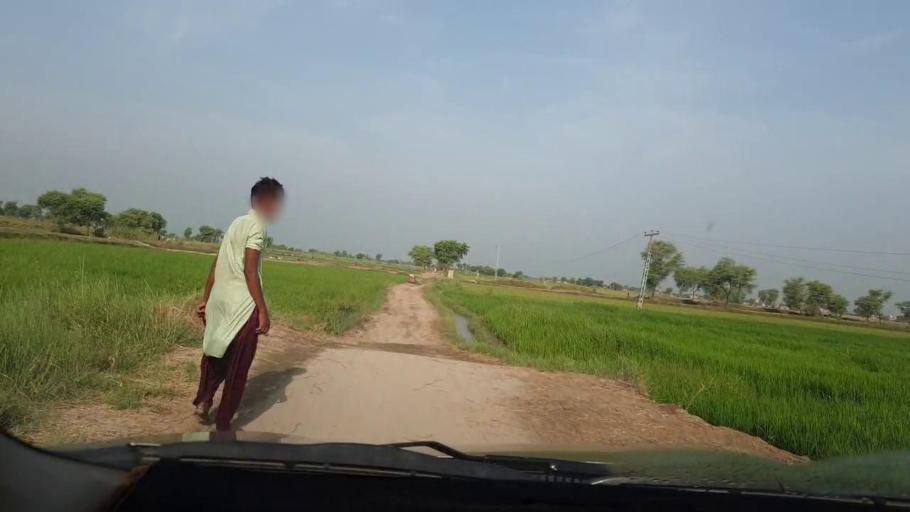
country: PK
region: Sindh
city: Goth Garelo
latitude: 27.4839
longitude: 68.0662
